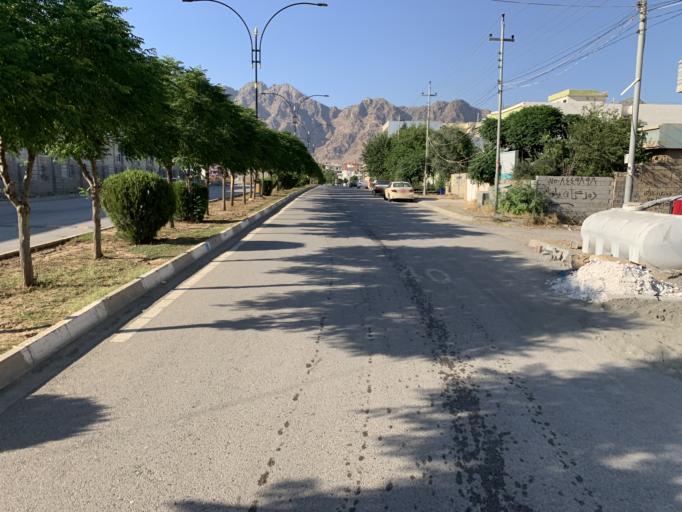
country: IQ
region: As Sulaymaniyah
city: Raniye
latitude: 36.2449
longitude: 44.8739
